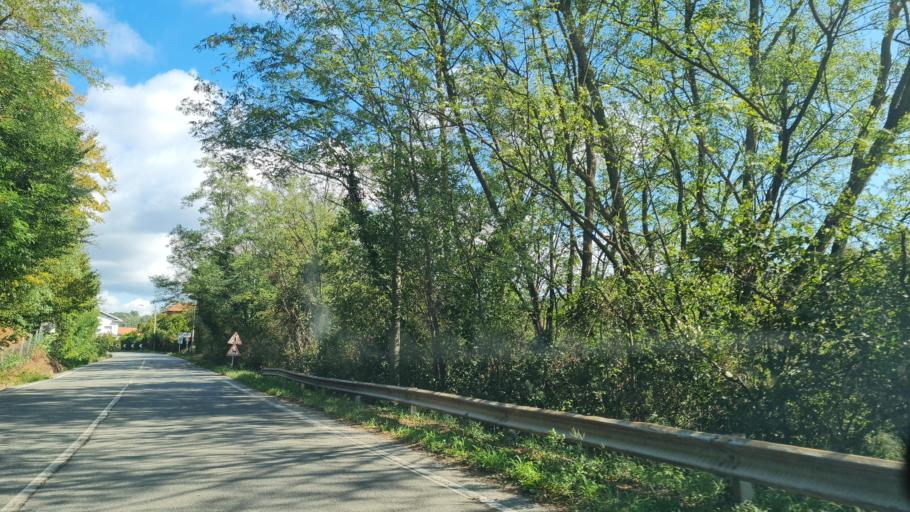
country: IT
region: Piedmont
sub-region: Provincia di Biella
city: Lessona
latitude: 45.5843
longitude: 8.1868
